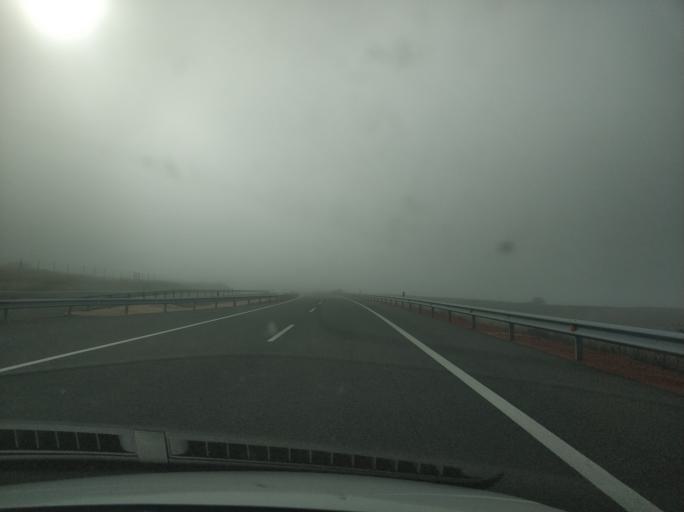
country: ES
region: Castille and Leon
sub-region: Provincia de Soria
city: Yelo
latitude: 41.2389
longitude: -2.4797
